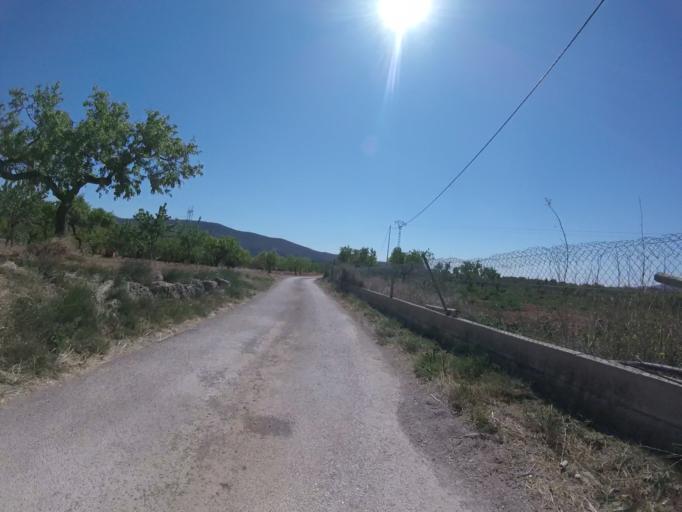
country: ES
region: Valencia
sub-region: Provincia de Castello
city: Cuevas de Vinroma
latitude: 40.3766
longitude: 0.1335
